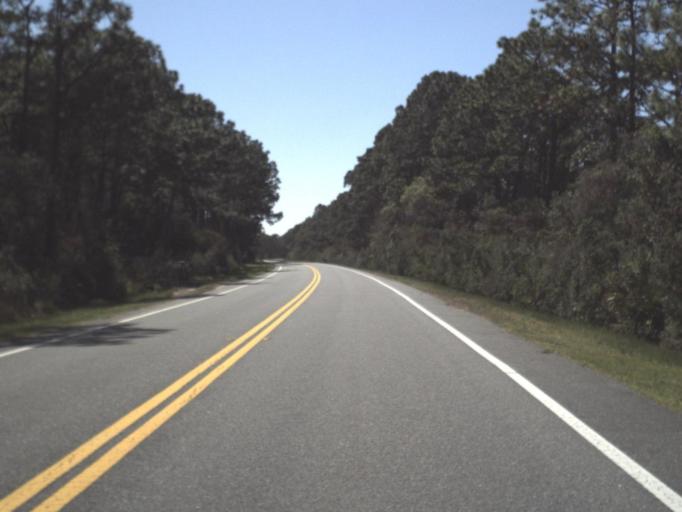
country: US
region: Florida
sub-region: Franklin County
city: Carrabelle
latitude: 29.9312
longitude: -84.4584
